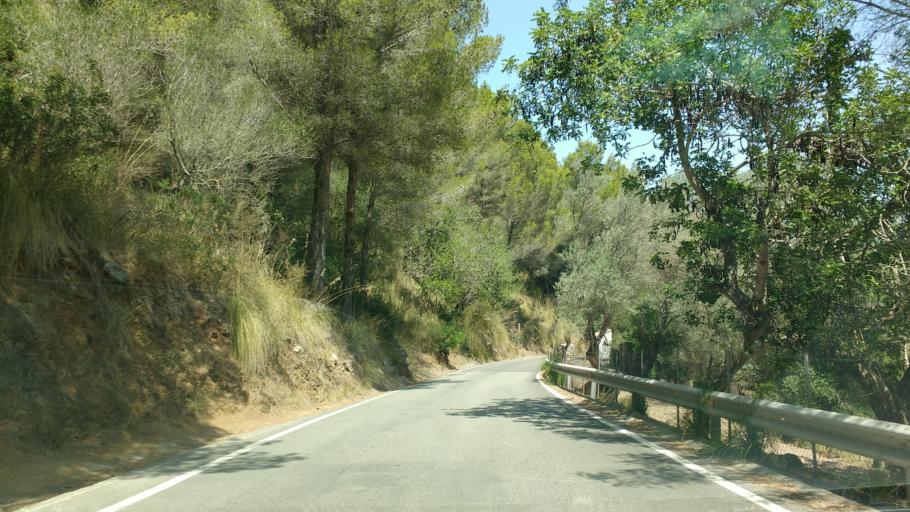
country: ES
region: Balearic Islands
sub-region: Illes Balears
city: Escorca
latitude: 39.8464
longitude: 2.7971
